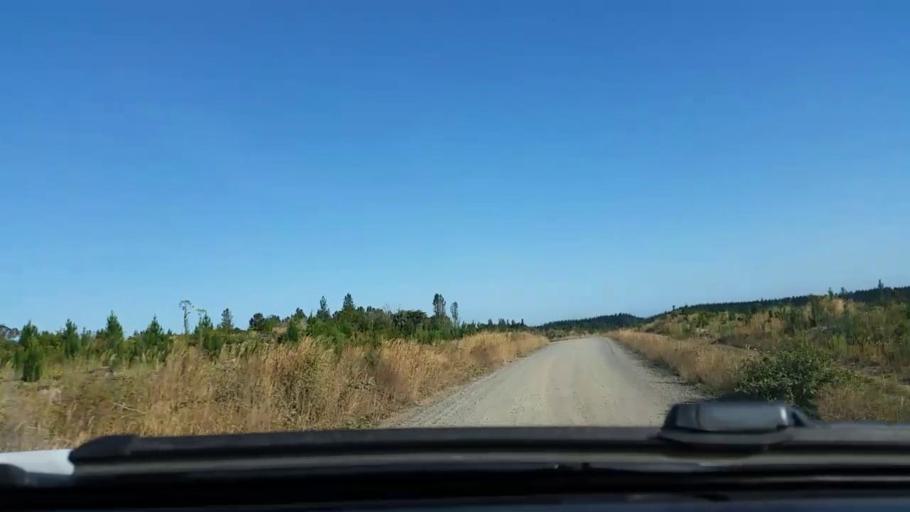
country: NZ
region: Bay of Plenty
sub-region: Kawerau District
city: Kawerau
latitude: -37.9981
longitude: 176.5405
